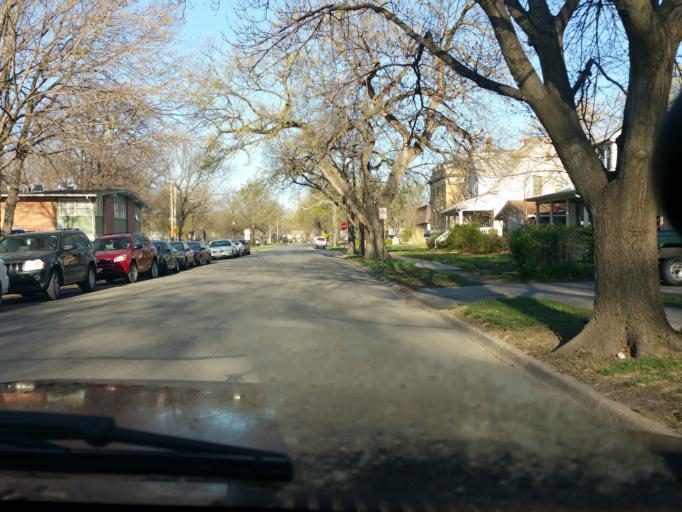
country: US
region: Kansas
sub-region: Riley County
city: Manhattan
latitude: 39.1838
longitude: -96.5721
